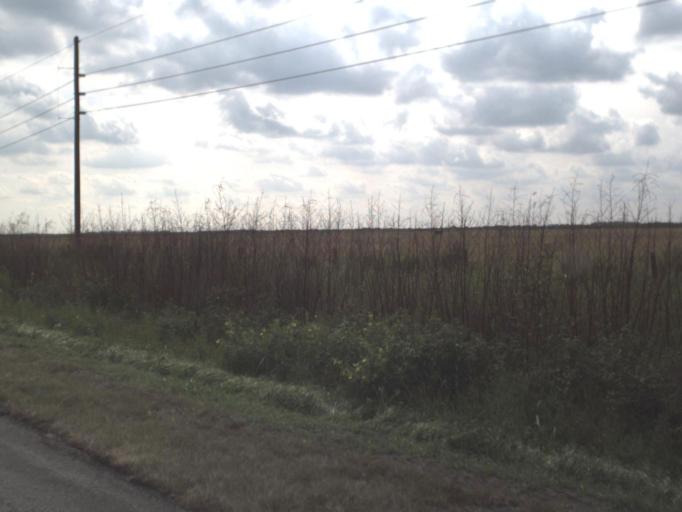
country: US
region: Florida
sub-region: Okeechobee County
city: Cypress Quarters
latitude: 27.4617
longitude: -80.8091
